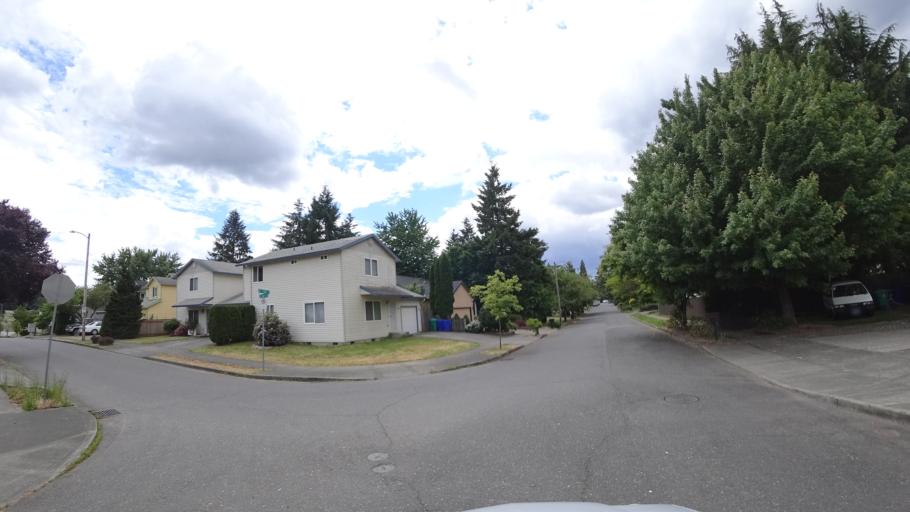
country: US
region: Oregon
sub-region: Clackamas County
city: Happy Valley
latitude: 45.4915
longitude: -122.5208
